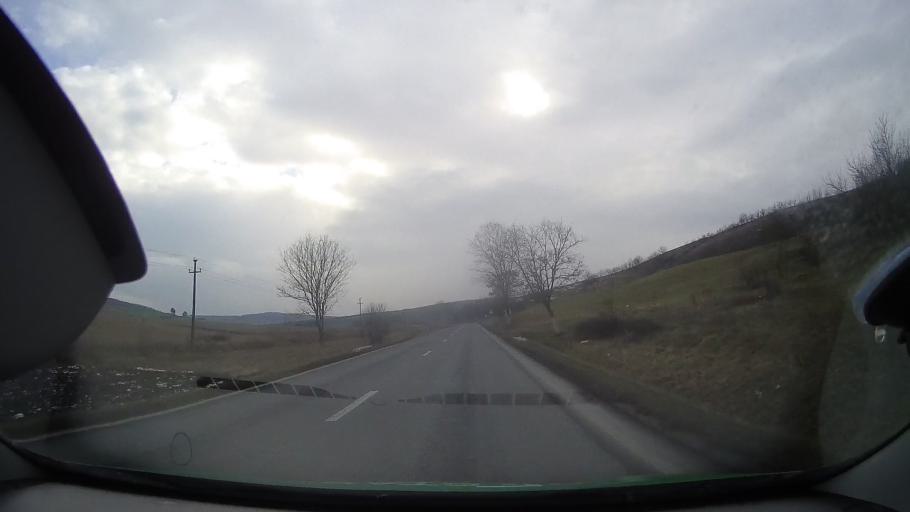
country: RO
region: Mures
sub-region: Comuna Cucerdea
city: Cucerdea
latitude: 46.3861
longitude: 24.2551
